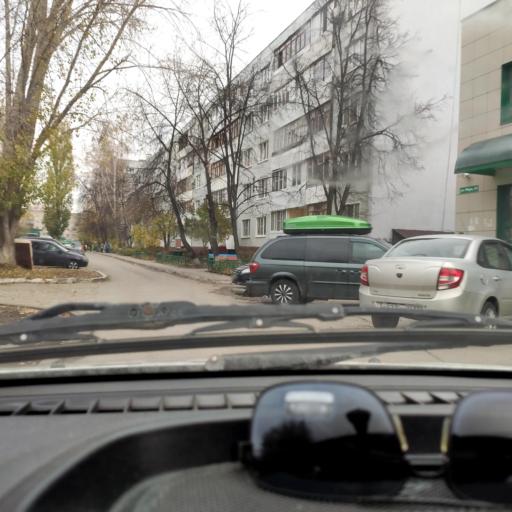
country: RU
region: Samara
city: Tol'yatti
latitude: 53.5084
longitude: 49.4369
